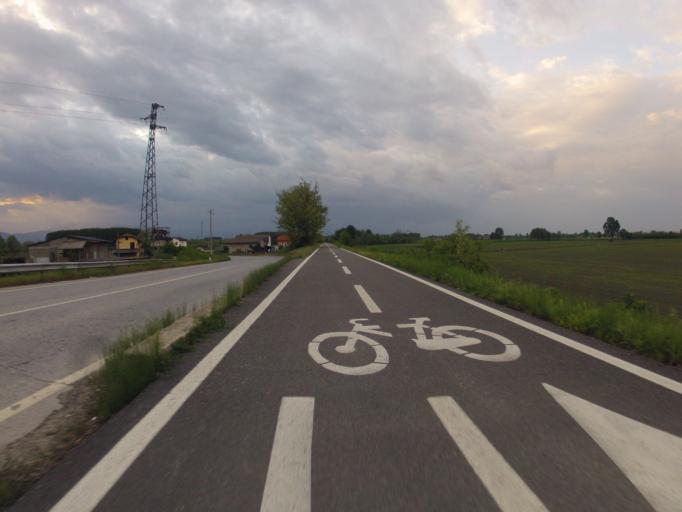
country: IT
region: Piedmont
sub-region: Provincia di Torino
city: Villafranca Piemonte
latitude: 44.8129
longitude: 7.4989
